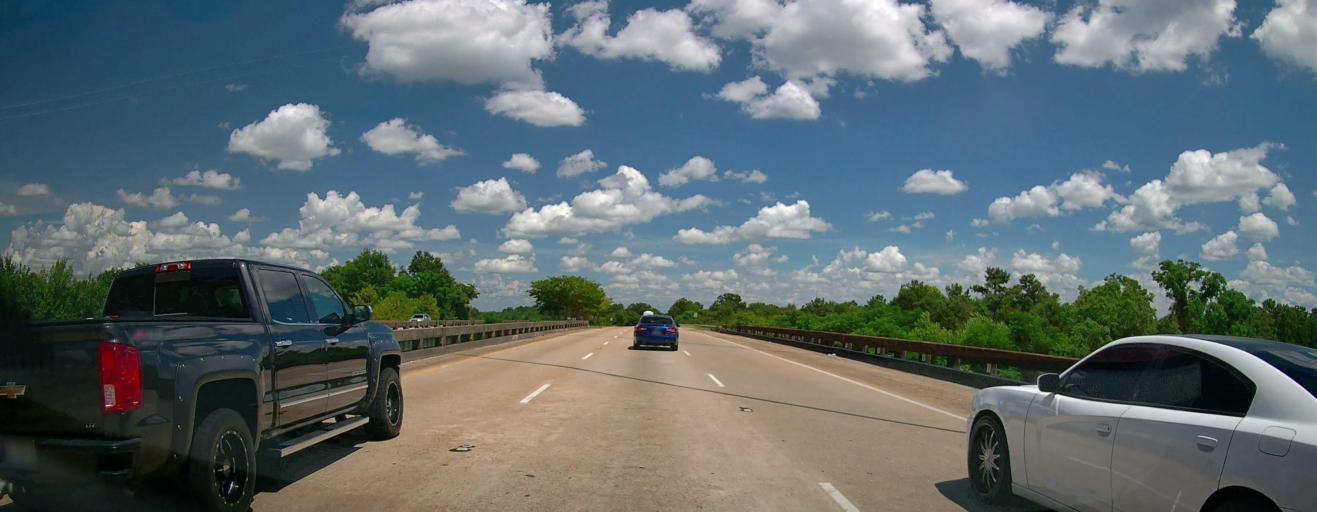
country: US
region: Alabama
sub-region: Montgomery County
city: Montgomery
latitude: 32.4240
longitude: -86.2809
